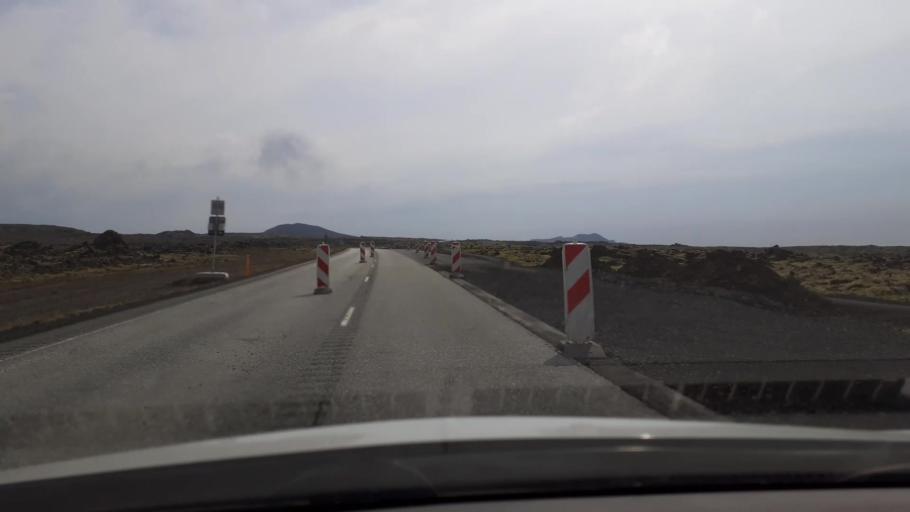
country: IS
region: Southern Peninsula
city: Vogar
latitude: 63.9142
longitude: -22.4210
